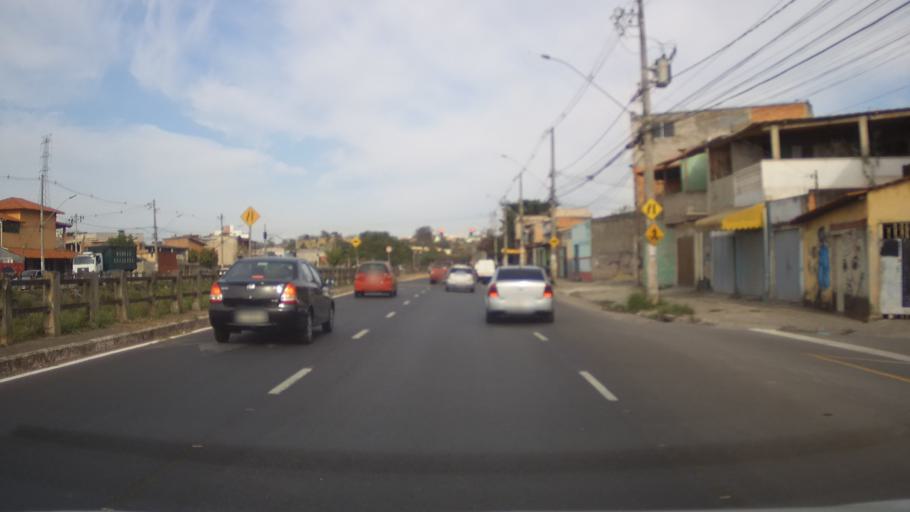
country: BR
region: Minas Gerais
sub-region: Contagem
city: Contagem
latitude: -19.8734
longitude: -44.0189
